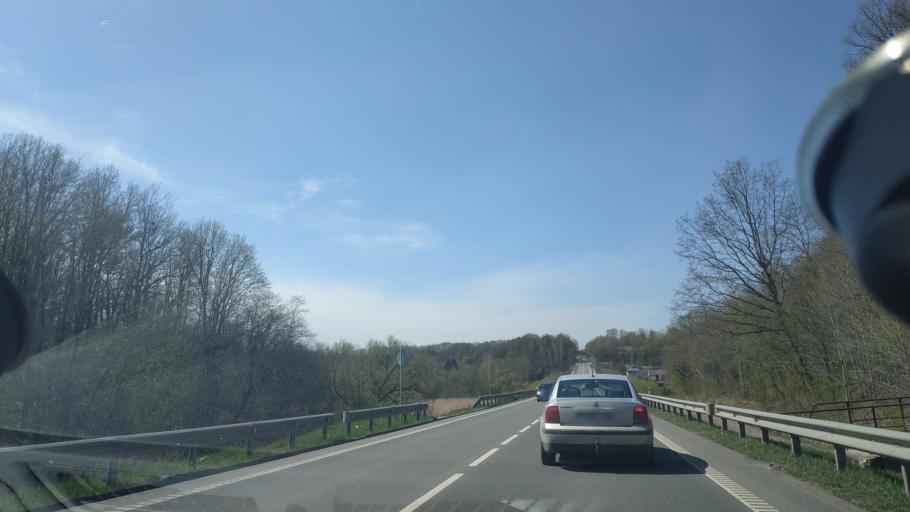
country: LT
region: Kauno apskritis
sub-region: Kaunas
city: Aleksotas
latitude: 54.8389
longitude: 23.9430
